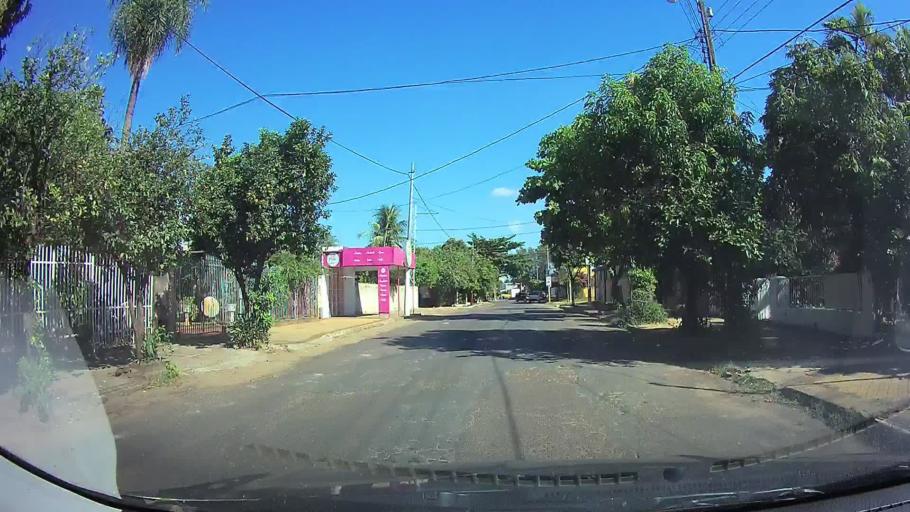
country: PY
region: Central
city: Fernando de la Mora
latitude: -25.3120
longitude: -57.5595
